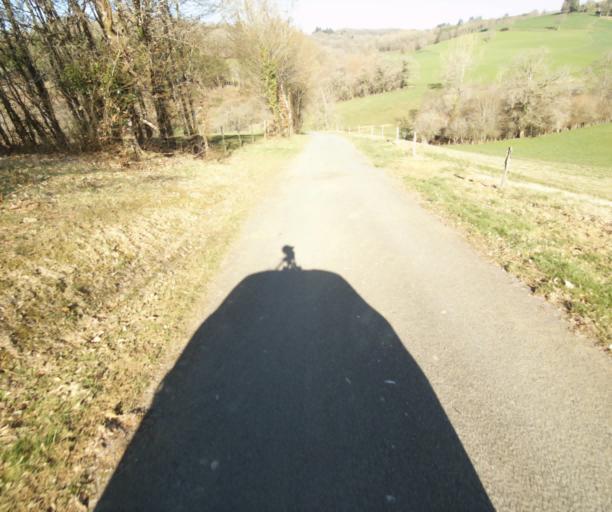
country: FR
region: Limousin
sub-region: Departement de la Correze
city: Seilhac
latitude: 45.3816
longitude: 1.7733
